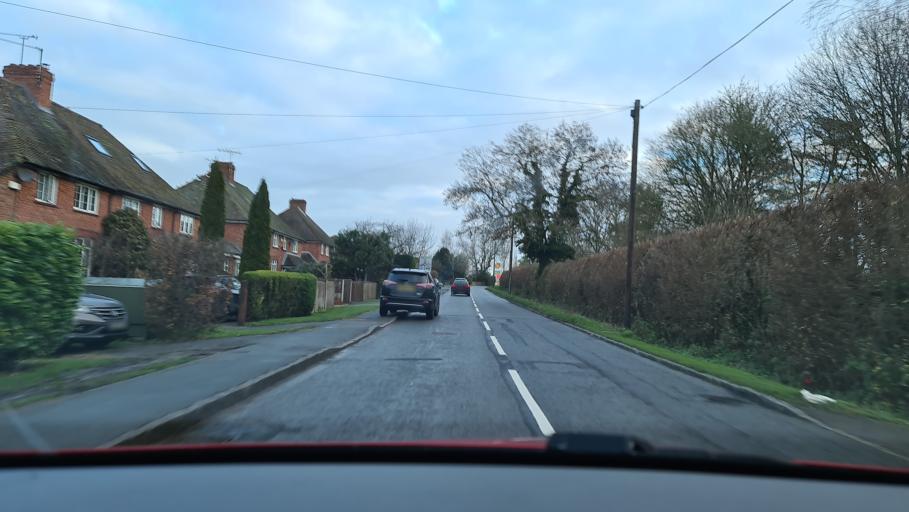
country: GB
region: England
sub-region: Buckinghamshire
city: Princes Risborough
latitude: 51.7330
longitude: -0.8536
